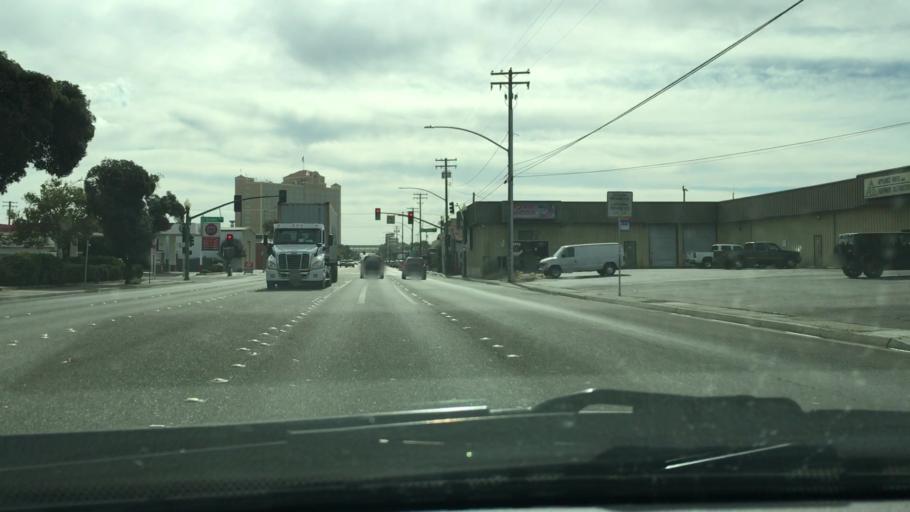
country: US
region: California
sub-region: Stanislaus County
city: Modesto
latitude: 37.6451
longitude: -121.0077
